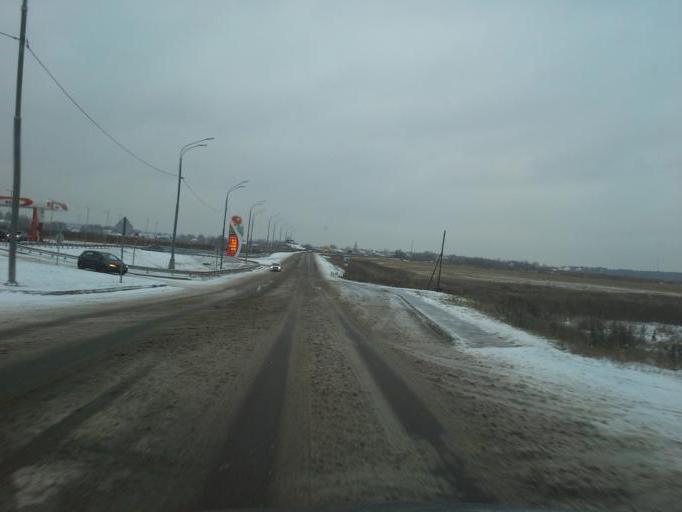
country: RU
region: Moskovskaya
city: Gorki Vtoryye
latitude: 55.7393
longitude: 37.1128
